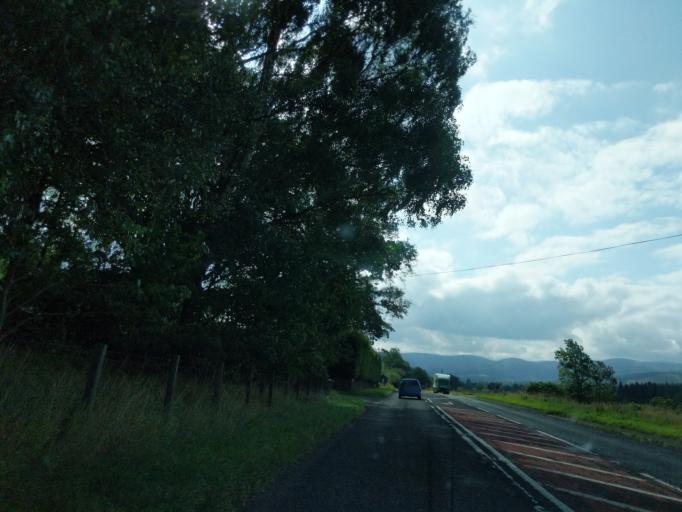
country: GB
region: Scotland
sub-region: The Scottish Borders
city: Peebles
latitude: 55.6749
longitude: -3.2029
